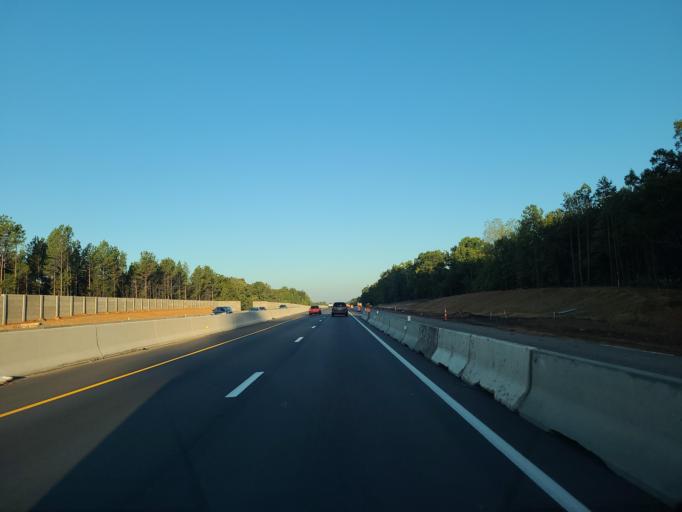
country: US
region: North Carolina
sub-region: Union County
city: Weddington
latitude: 35.0610
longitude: -80.7797
